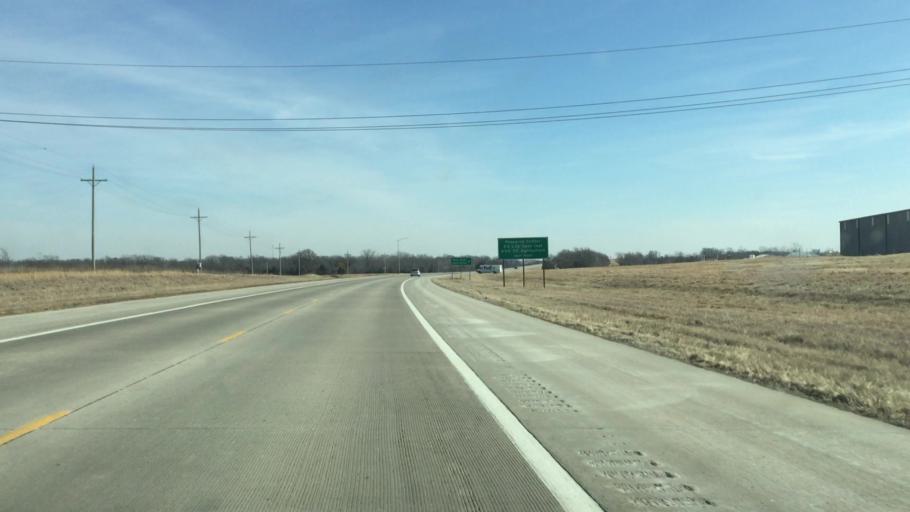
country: US
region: Kansas
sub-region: Labette County
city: Parsons
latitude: 37.3692
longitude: -95.2889
